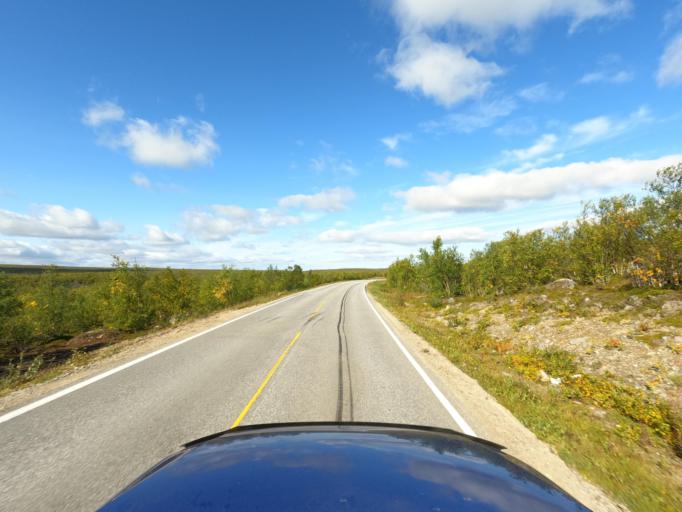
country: NO
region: Finnmark Fylke
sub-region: Karasjok
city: Karasjohka
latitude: 69.5309
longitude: 25.4389
